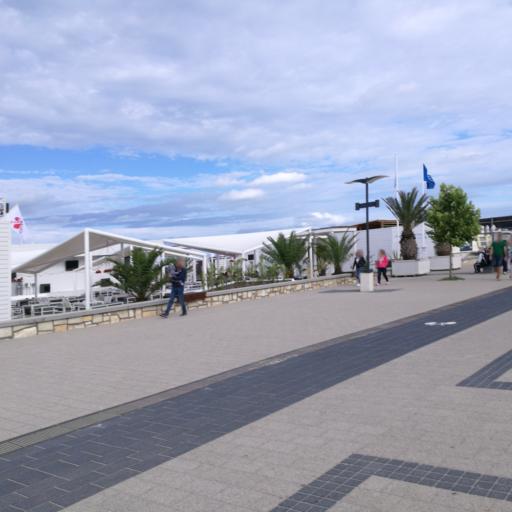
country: RO
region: Constanta
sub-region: Municipiul Constanta
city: Palazu Mare
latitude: 44.2434
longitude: 28.6231
